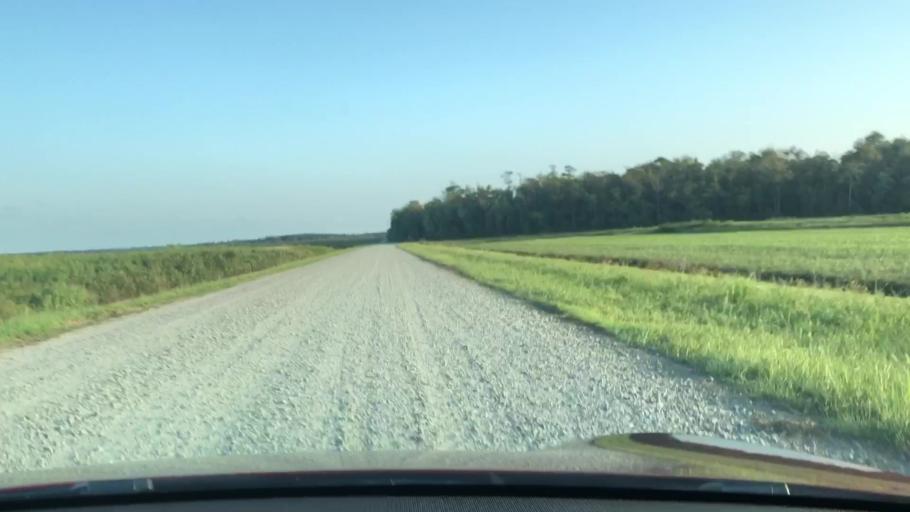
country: US
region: North Carolina
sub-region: Dare County
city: Manteo
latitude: 35.8468
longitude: -75.8609
